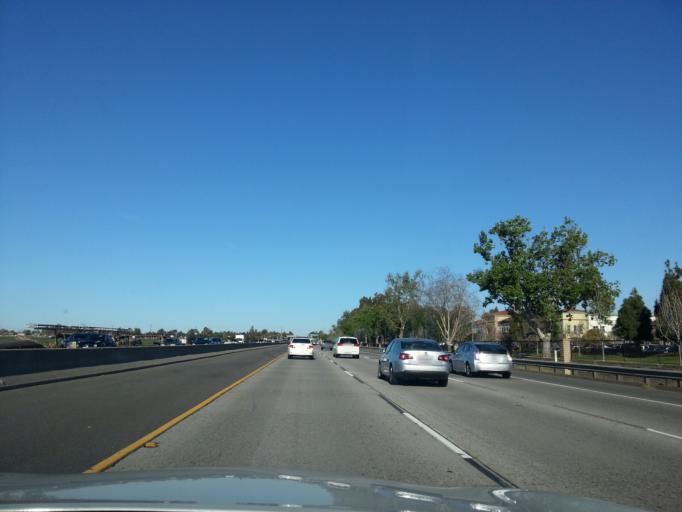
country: US
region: California
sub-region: Ventura County
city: Camarillo
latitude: 34.2104
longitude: -118.9974
